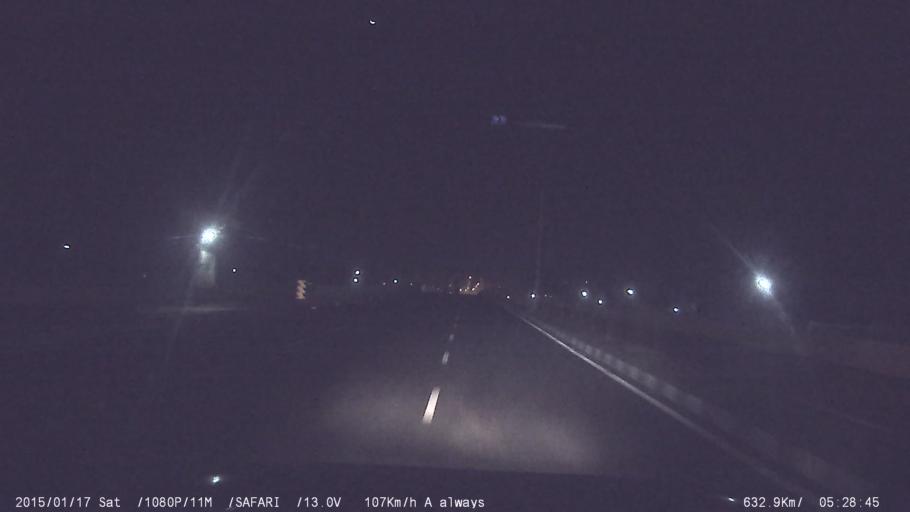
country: IN
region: Tamil Nadu
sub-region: Vellore
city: Arcot
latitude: 12.9227
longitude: 79.2763
